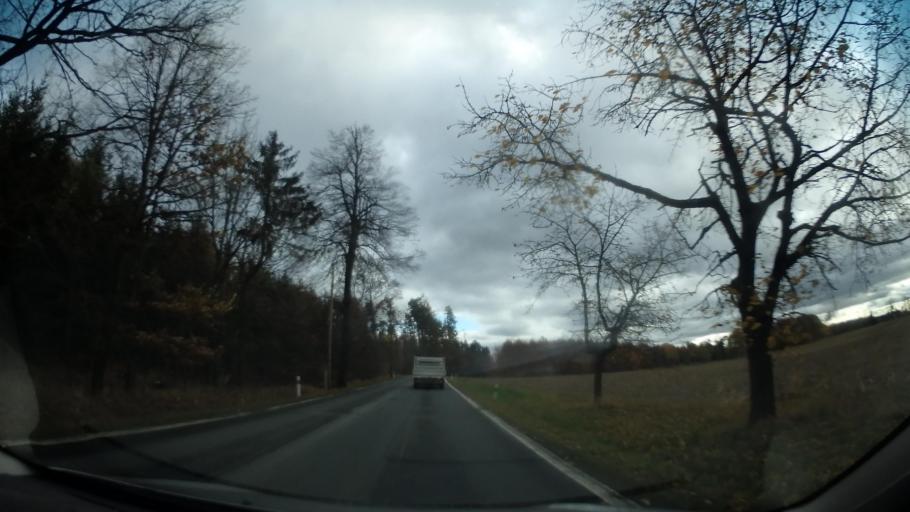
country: CZ
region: Vysocina
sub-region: Okres Zd'ar nad Sazavou
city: Velka Bites
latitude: 49.2662
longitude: 16.2449
